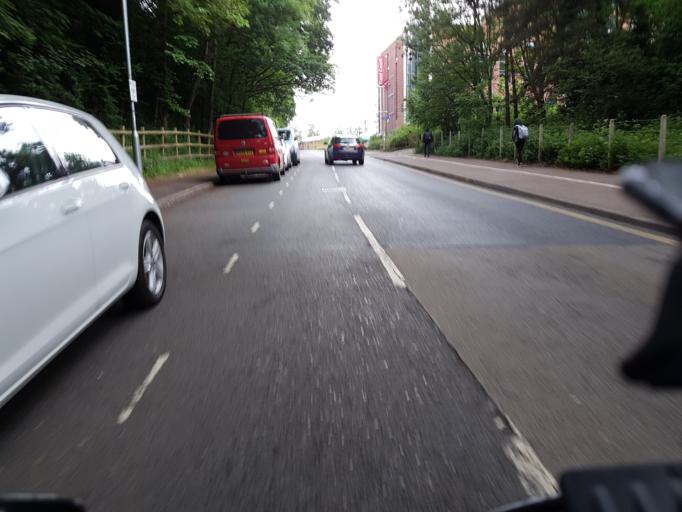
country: GB
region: England
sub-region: Devon
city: Exeter
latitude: 50.7349
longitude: -3.5305
